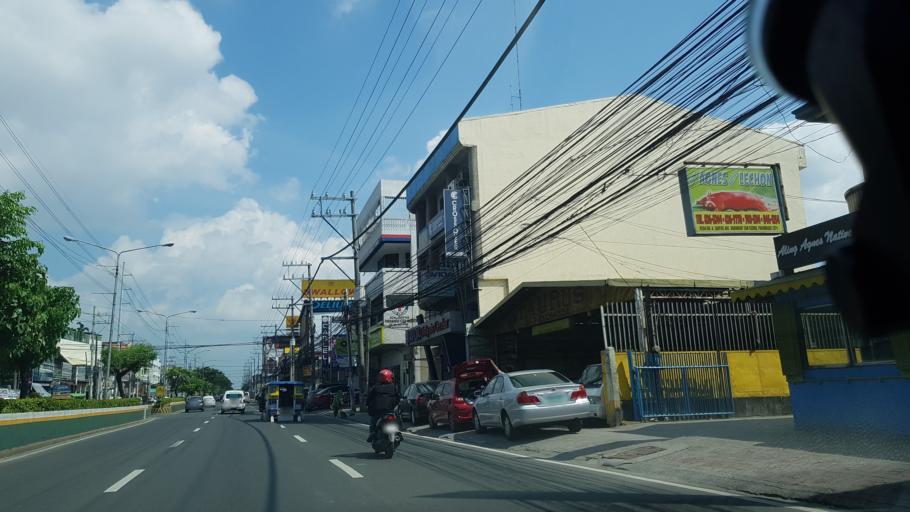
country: PH
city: Sambayanihan People's Village
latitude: 14.4737
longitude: 121.0033
